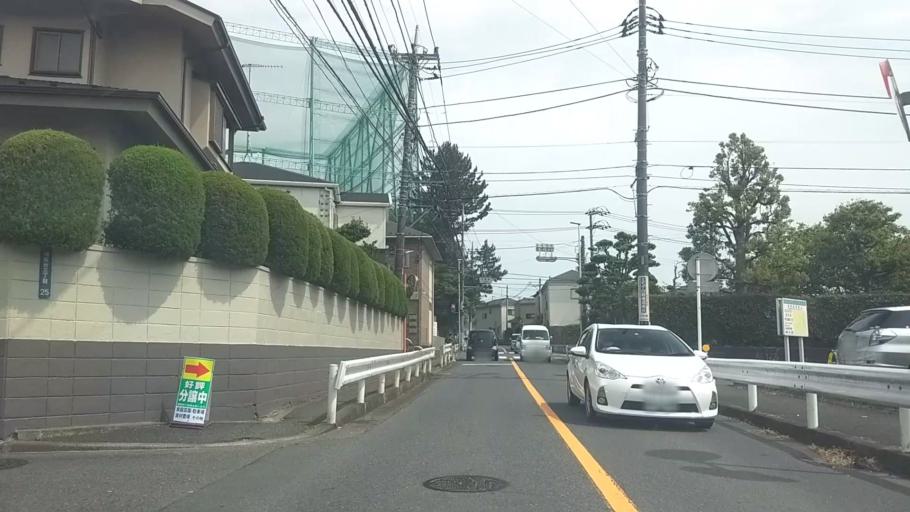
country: JP
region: Kanagawa
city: Fujisawa
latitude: 35.3891
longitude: 139.4626
